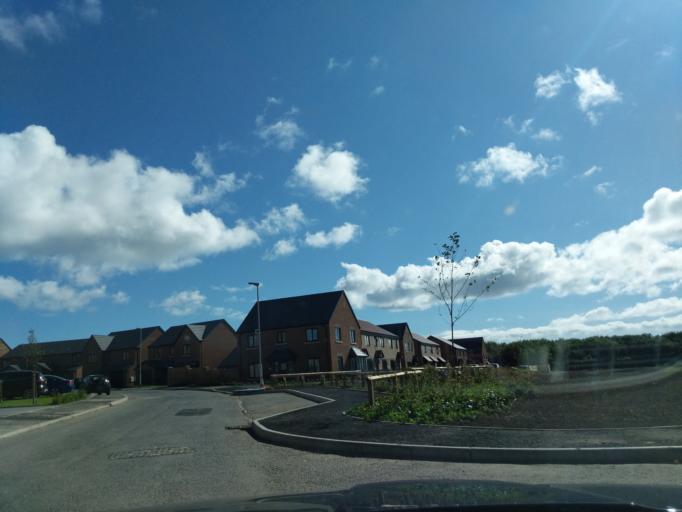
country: GB
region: England
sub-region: Northumberland
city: Newbiggin-by-the-Sea
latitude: 55.1690
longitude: -1.5460
